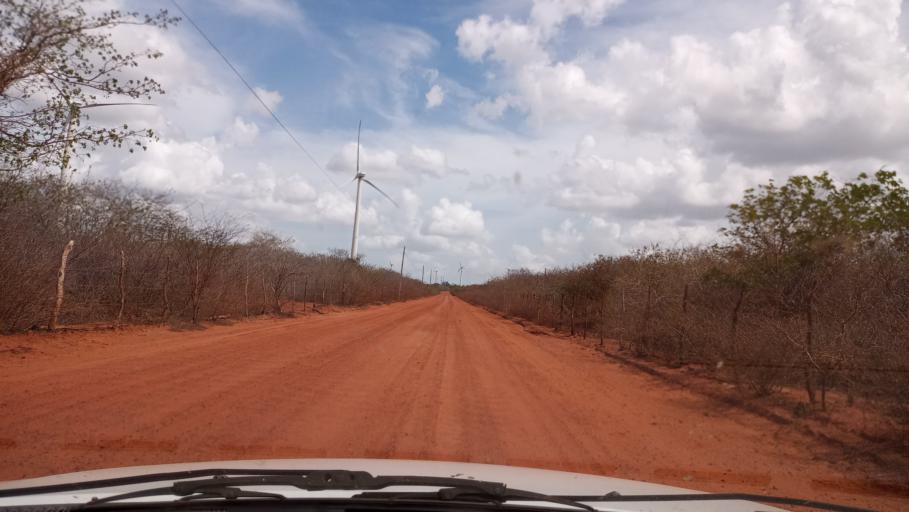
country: BR
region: Rio Grande do Norte
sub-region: Joao Camara
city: Joao Camara
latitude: -5.3886
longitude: -35.8640
